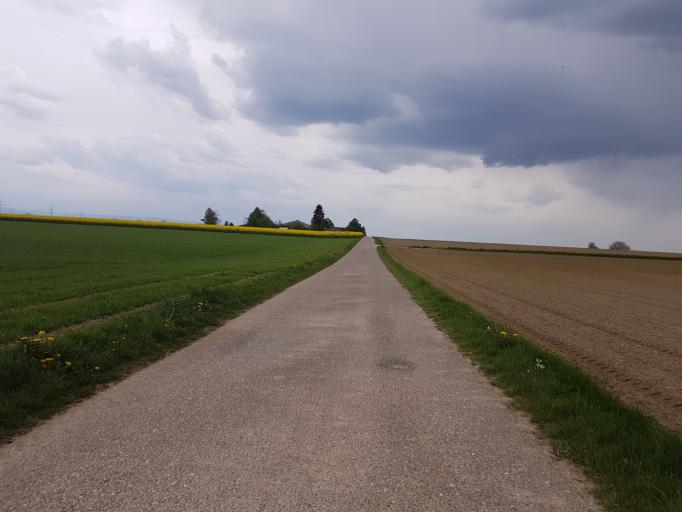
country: DE
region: Baden-Wuerttemberg
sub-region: Regierungsbezirk Stuttgart
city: Bondorf
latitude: 48.5157
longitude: 8.8082
